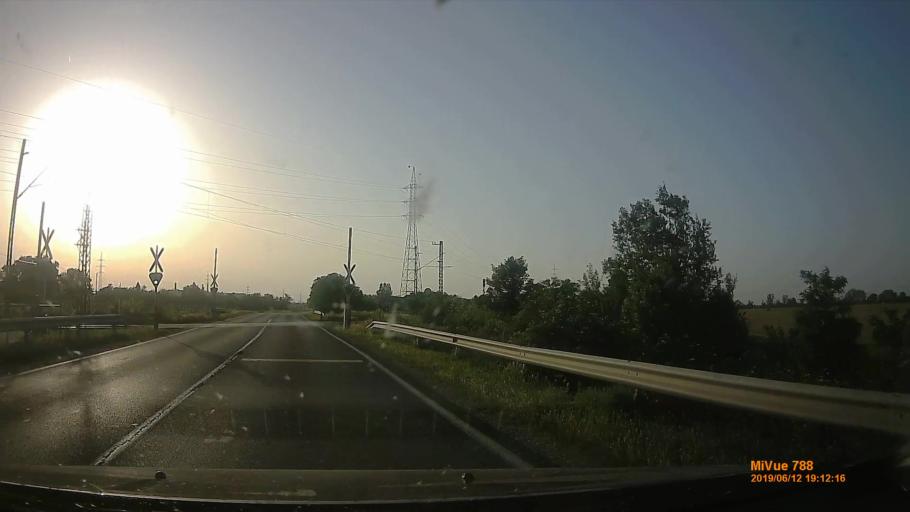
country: HU
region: Bacs-Kiskun
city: Varosfoeld
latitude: 46.8567
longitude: 19.7360
